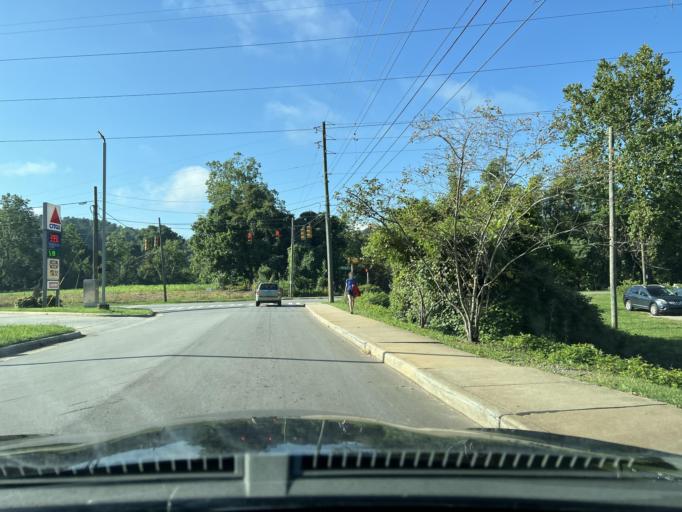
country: US
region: North Carolina
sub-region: Buncombe County
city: Asheville
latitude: 35.5671
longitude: -82.5738
